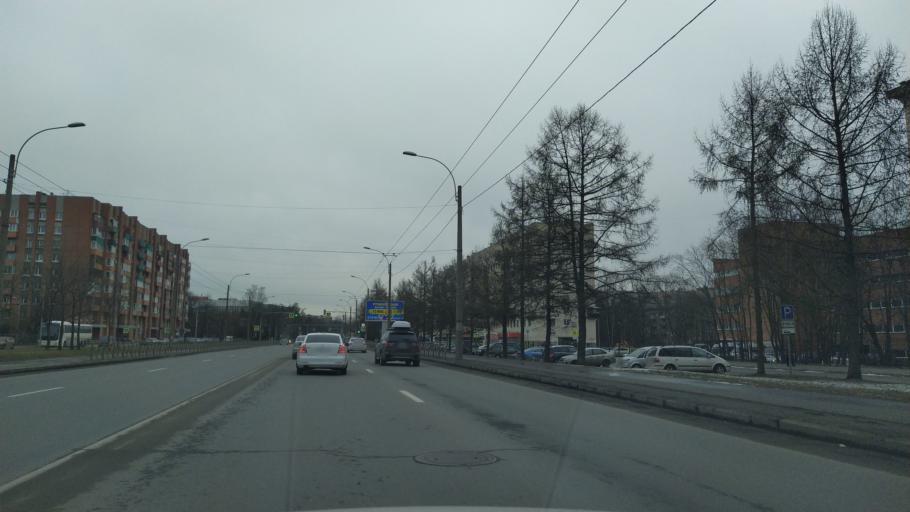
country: RU
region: St.-Petersburg
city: Sosnovka
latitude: 60.0089
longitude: 30.3503
